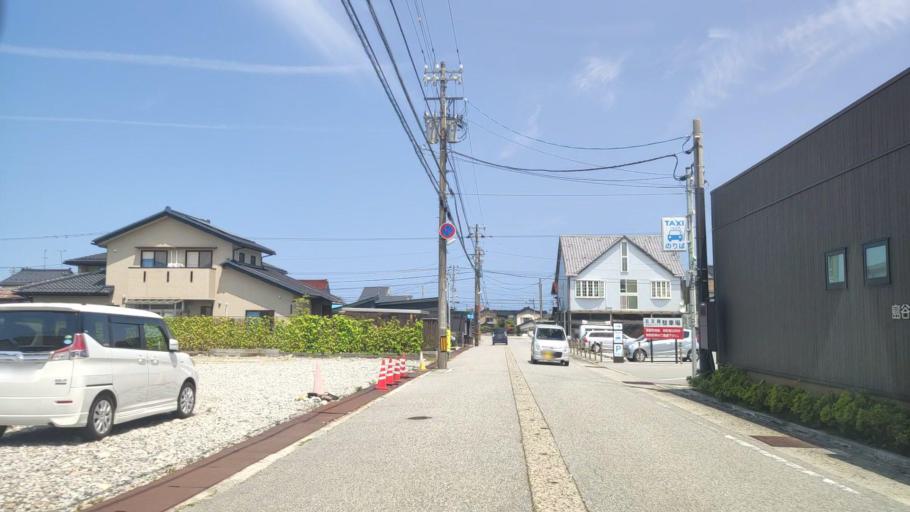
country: JP
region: Toyama
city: Nyuzen
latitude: 36.9572
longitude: 137.5593
